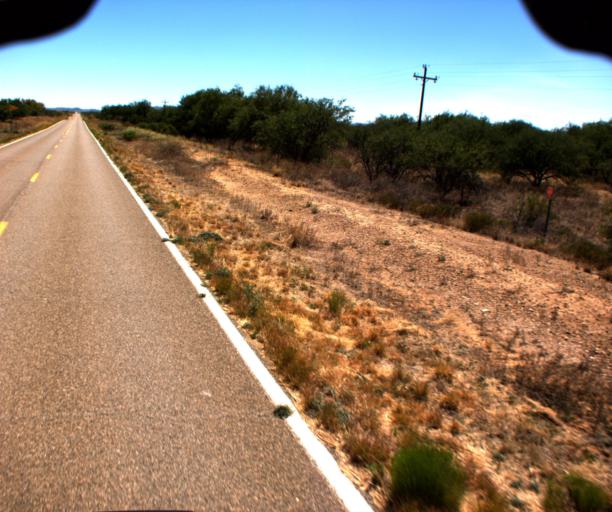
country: US
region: Arizona
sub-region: Pima County
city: Arivaca Junction
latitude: 31.6311
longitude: -111.5076
